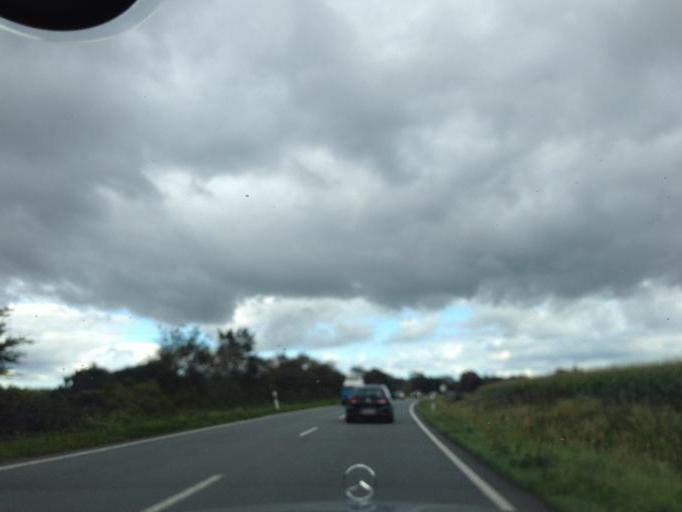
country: DE
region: Schleswig-Holstein
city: Horup
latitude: 54.7500
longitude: 9.0873
